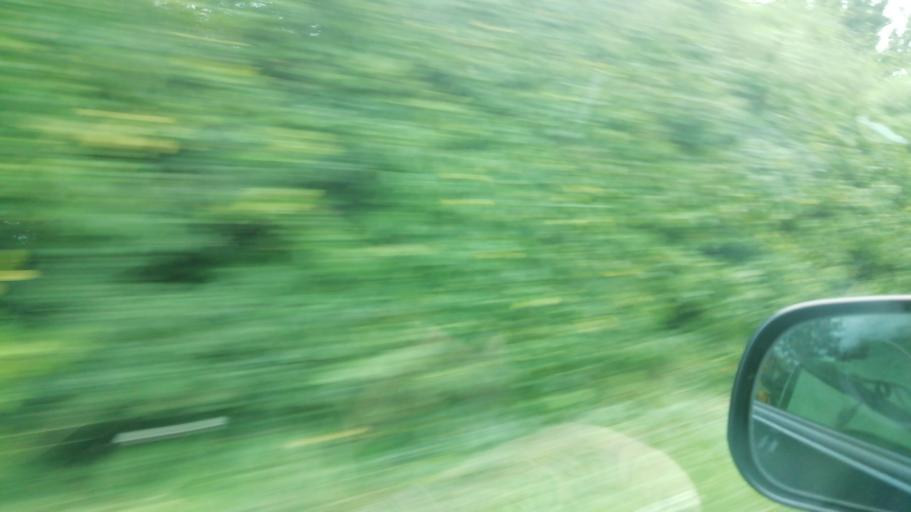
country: IE
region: Munster
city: Fethard
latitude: 52.5237
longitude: -7.6825
